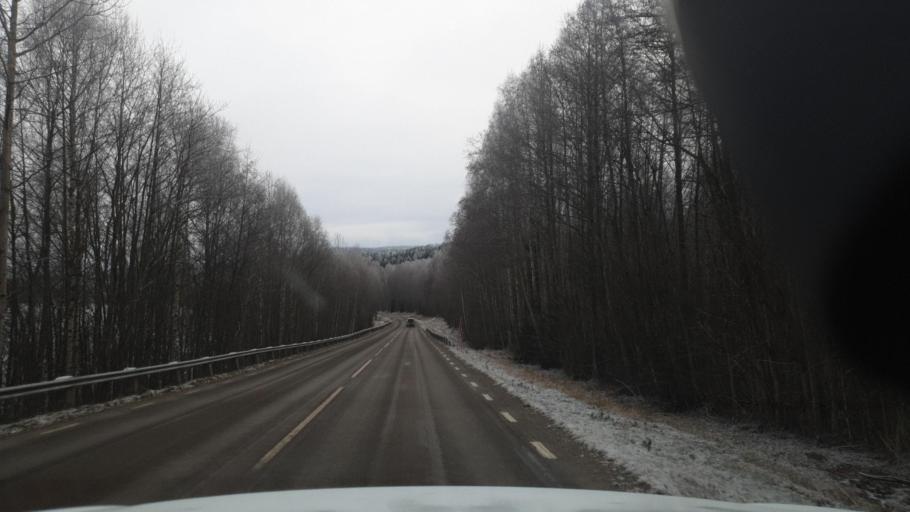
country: SE
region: Vaermland
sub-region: Eda Kommun
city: Amotfors
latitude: 59.6943
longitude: 12.3430
